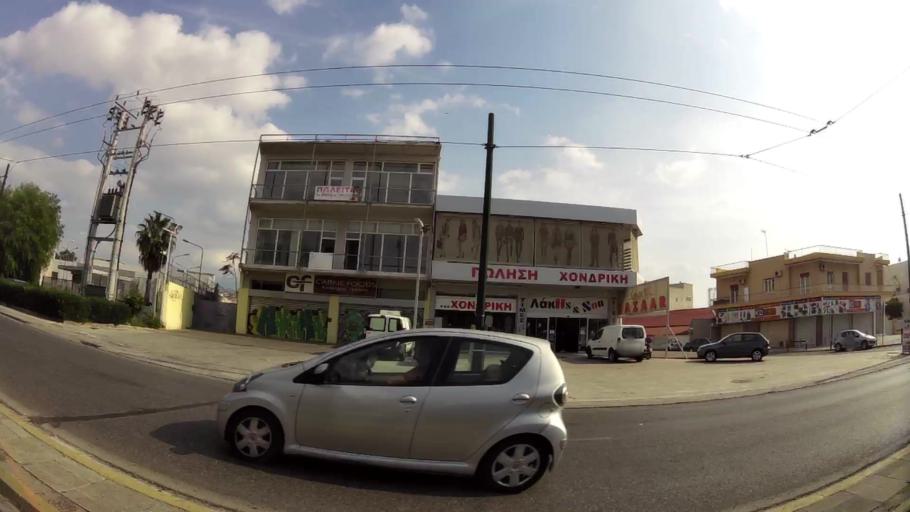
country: GR
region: Attica
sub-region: Nomarchia Athinas
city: Tavros
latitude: 37.9630
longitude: 23.6915
